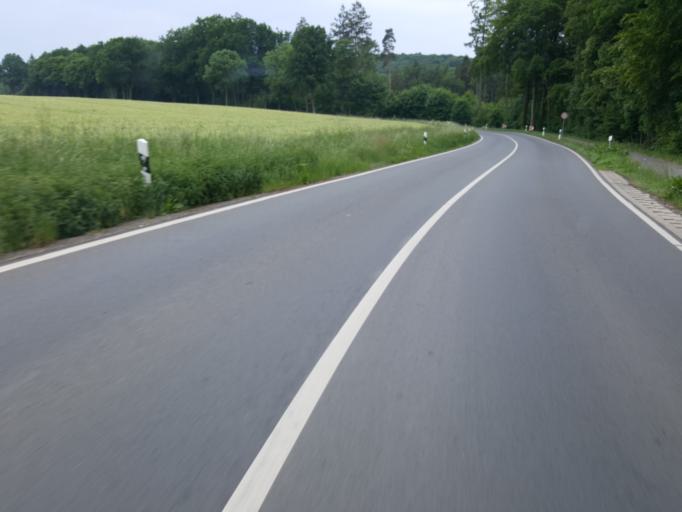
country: DE
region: Lower Saxony
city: Rehburg-Loccum
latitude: 52.4495
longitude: 9.2194
